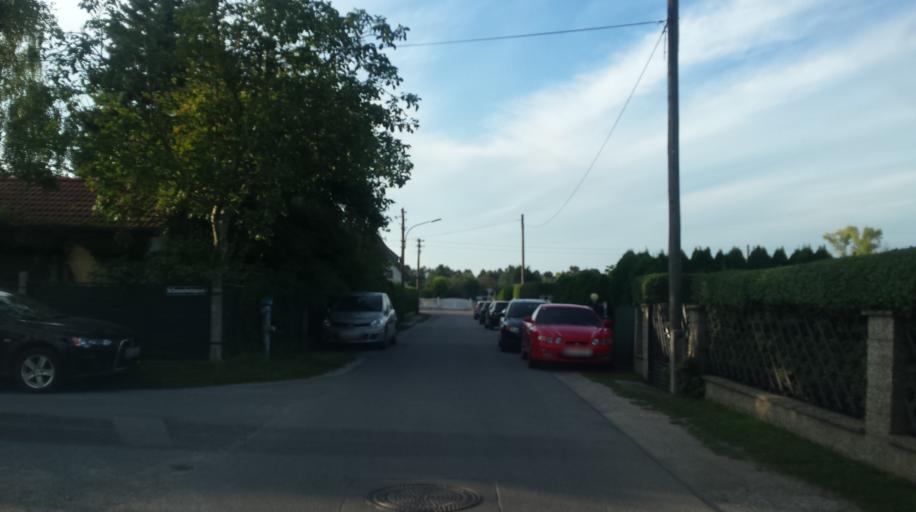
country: AT
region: Lower Austria
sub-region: Politischer Bezirk Ganserndorf
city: Parbasdorf
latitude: 48.3134
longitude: 16.6247
